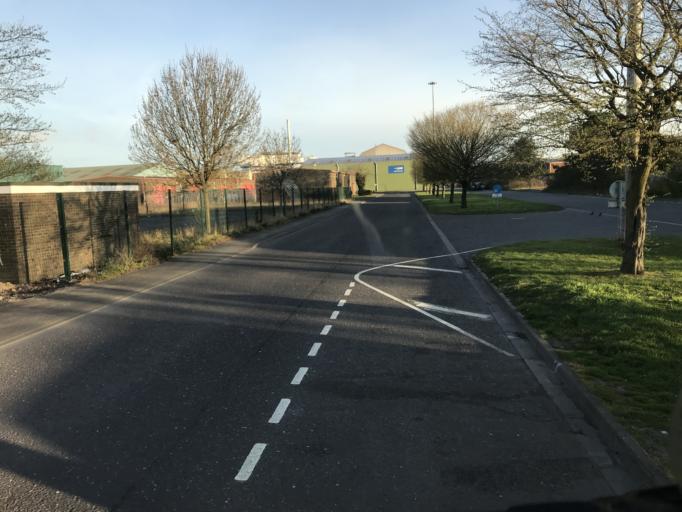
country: GB
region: England
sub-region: North Lincolnshire
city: Burton upon Stather
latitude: 53.6193
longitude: -0.6976
